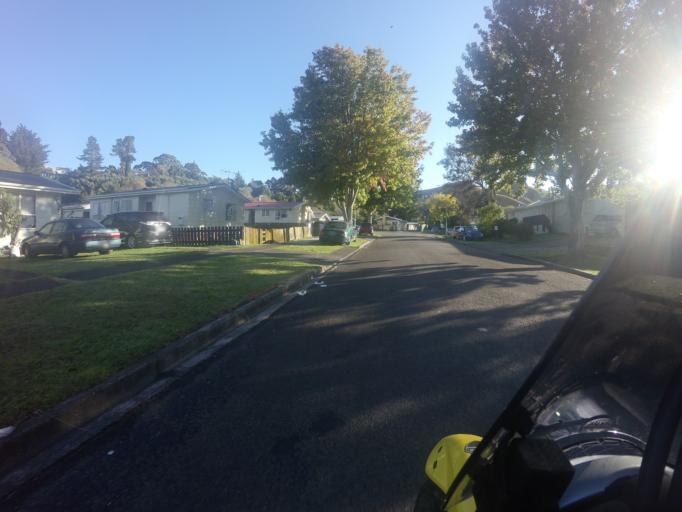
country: NZ
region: Gisborne
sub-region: Gisborne District
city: Gisborne
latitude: -38.6667
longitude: 178.0572
